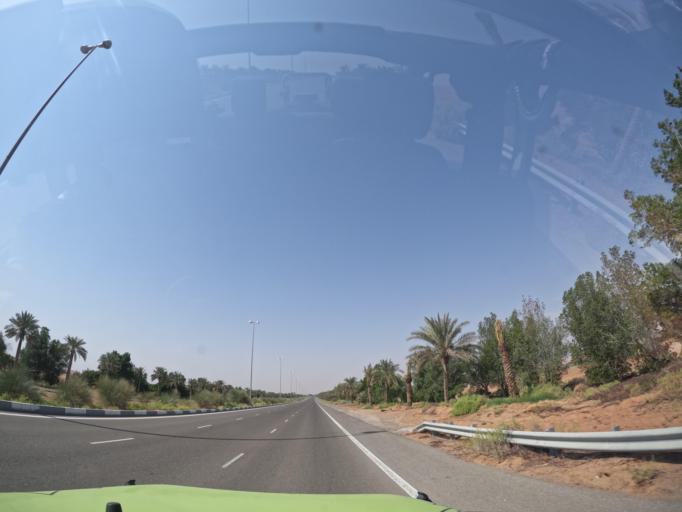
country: AE
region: Abu Dhabi
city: Al Ain
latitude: 24.2133
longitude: 55.6089
